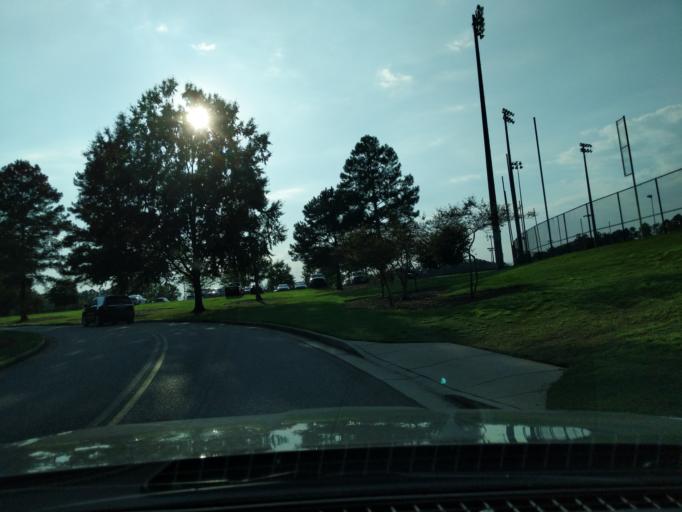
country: US
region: South Carolina
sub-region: Aiken County
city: North Augusta
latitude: 33.5001
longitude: -81.9827
